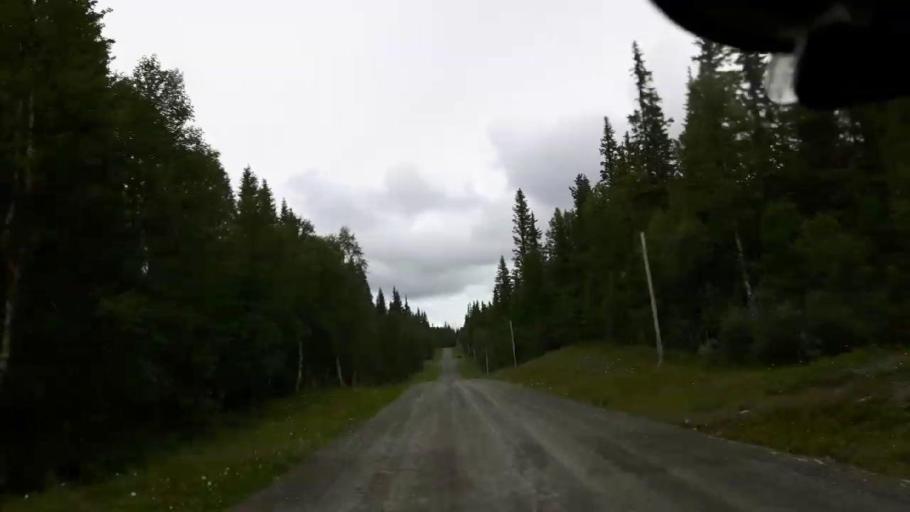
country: SE
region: Jaemtland
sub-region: Krokoms Kommun
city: Valla
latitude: 63.7478
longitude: 13.8354
